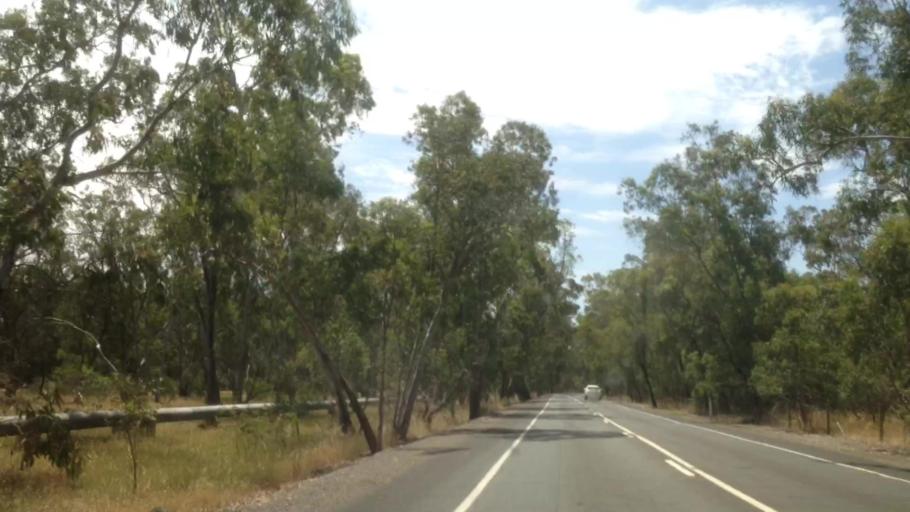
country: AU
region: South Australia
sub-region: Adelaide Hills
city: Birdwood
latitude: -34.7453
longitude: 138.9635
